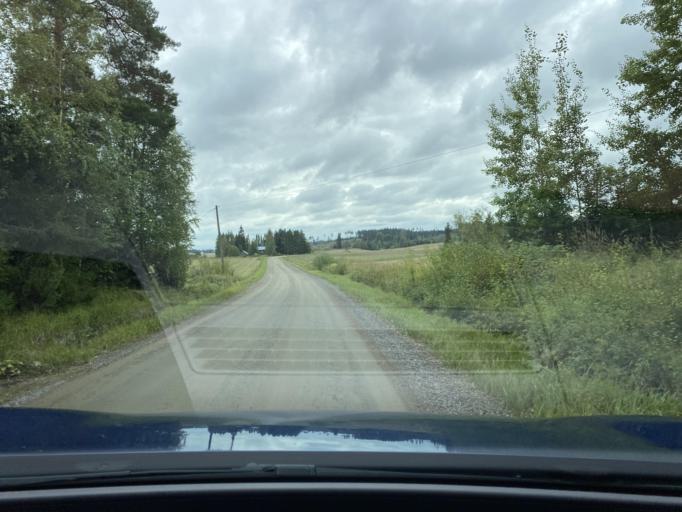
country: FI
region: Pirkanmaa
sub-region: Lounais-Pirkanmaa
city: Punkalaidun
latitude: 61.1873
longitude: 23.1837
